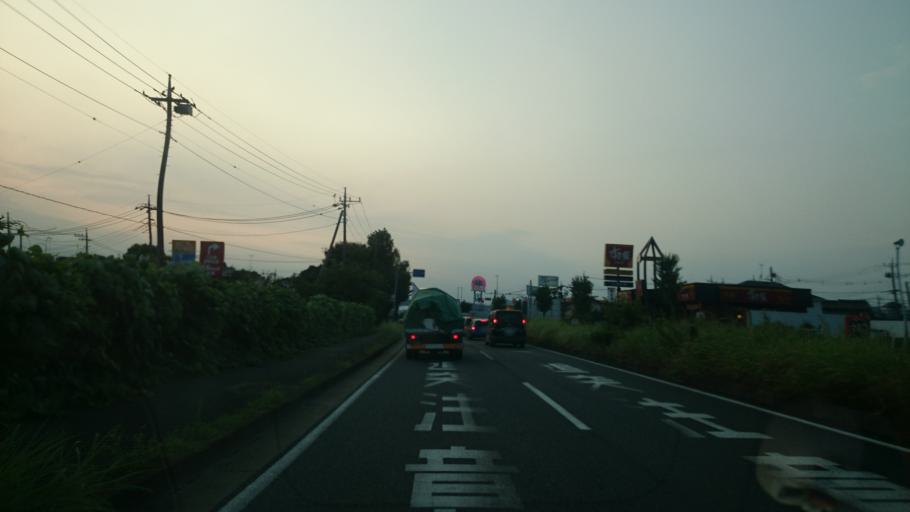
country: JP
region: Saitama
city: Iwatsuki
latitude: 35.9484
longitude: 139.6716
